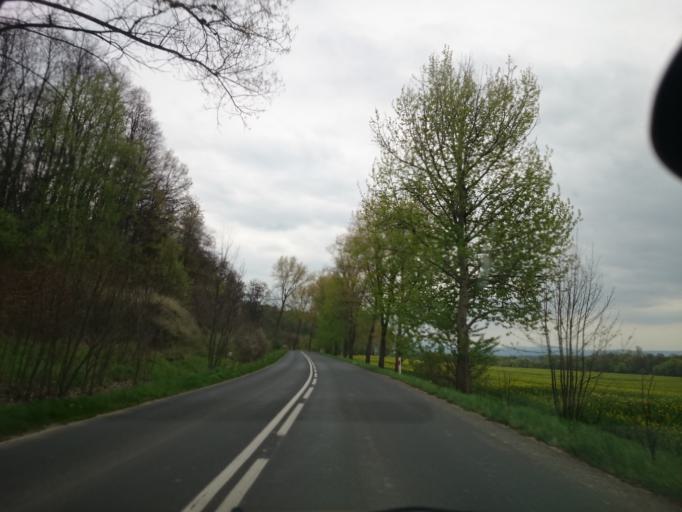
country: PL
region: Opole Voivodeship
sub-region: Powiat nyski
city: Nysa
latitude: 50.4011
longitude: 17.3432
